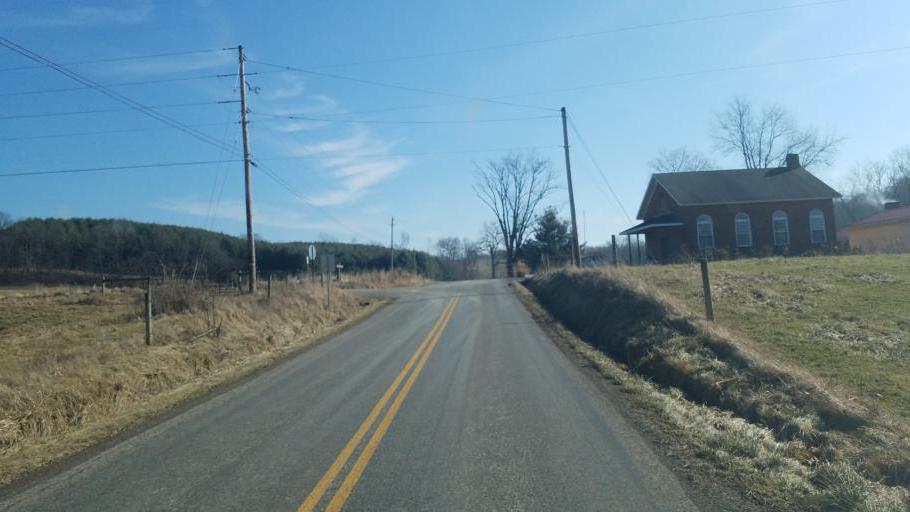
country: US
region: Ohio
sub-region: Holmes County
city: Millersburg
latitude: 40.5768
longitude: -81.8788
